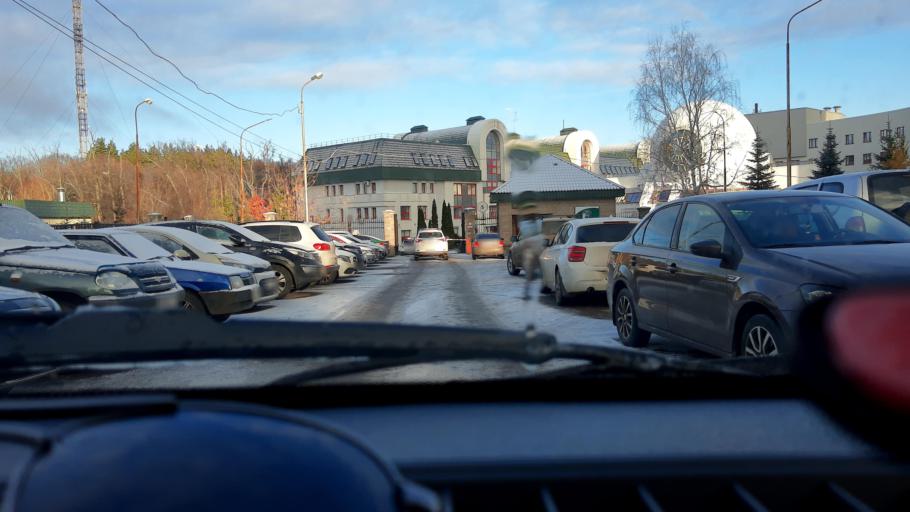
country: RU
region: Bashkortostan
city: Ufa
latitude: 54.7707
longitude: 56.0092
